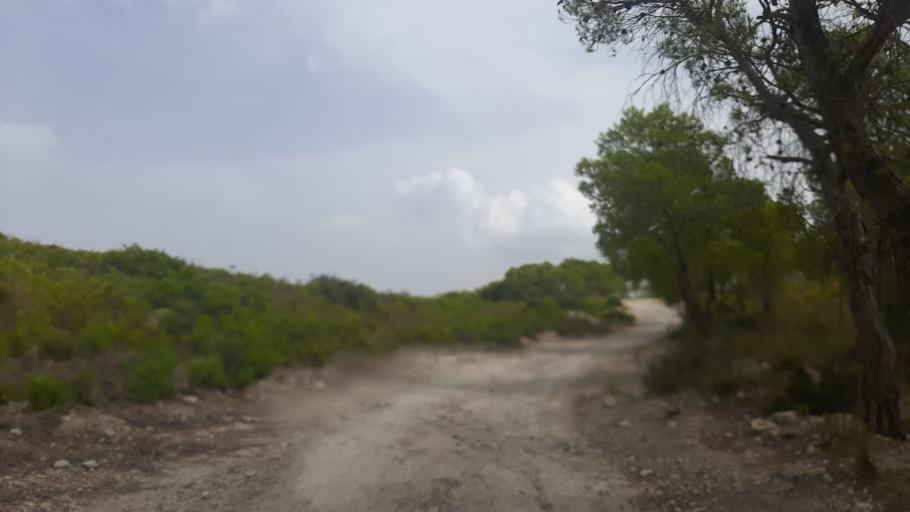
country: TN
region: Zaghwan
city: El Fahs
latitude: 36.1960
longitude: 9.8522
